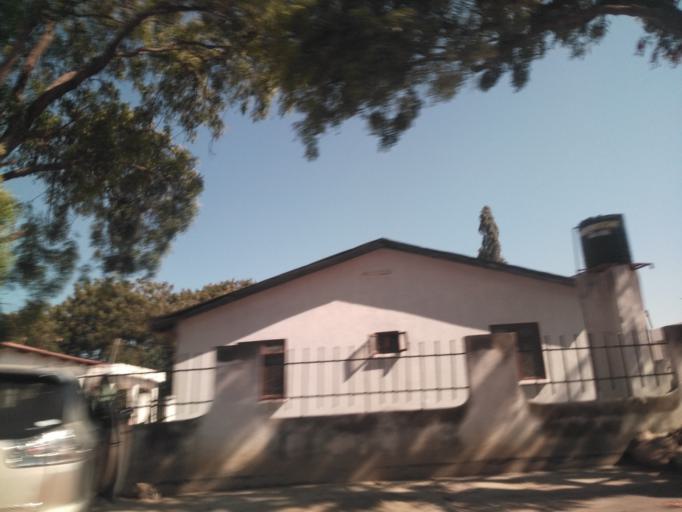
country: TZ
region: Dodoma
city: Dodoma
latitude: -6.1609
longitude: 35.7499
